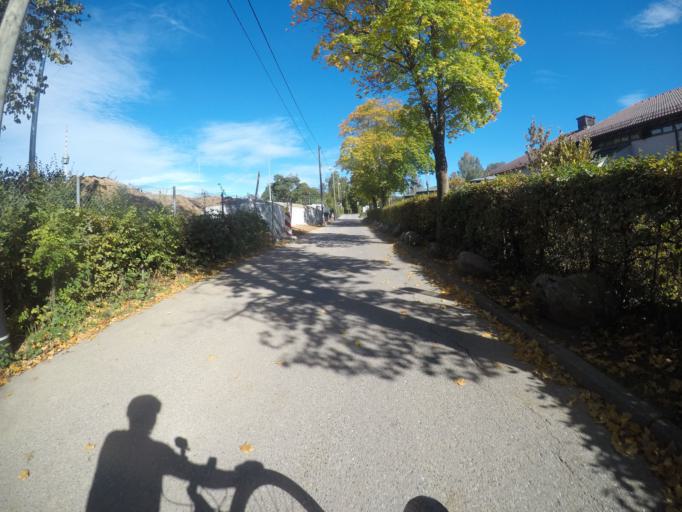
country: DE
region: Baden-Wuerttemberg
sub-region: Regierungsbezirk Stuttgart
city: Stuttgart
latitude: 48.7495
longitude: 9.1885
